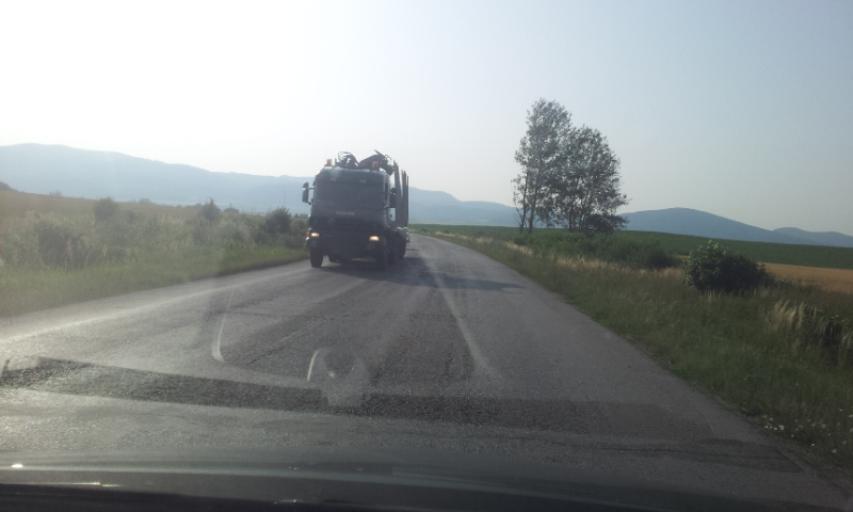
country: SK
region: Kosicky
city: Kosice
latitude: 48.6085
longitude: 21.2915
